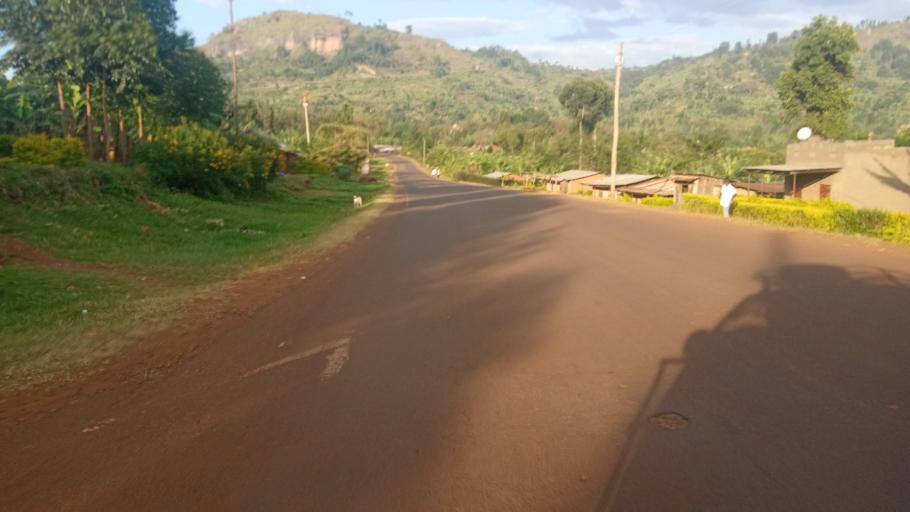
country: UG
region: Eastern Region
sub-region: Kapchorwa District
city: Kapchorwa
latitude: 1.3249
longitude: 34.3538
